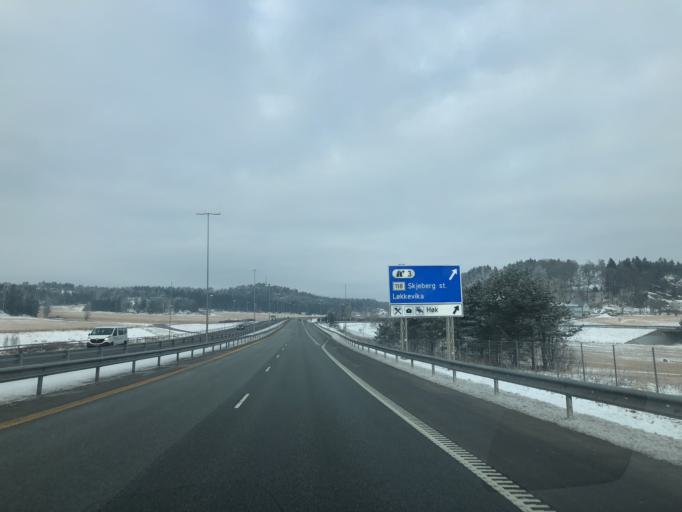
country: NO
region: Ostfold
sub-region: Sarpsborg
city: Skjeberg
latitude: 59.1768
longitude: 11.2093
